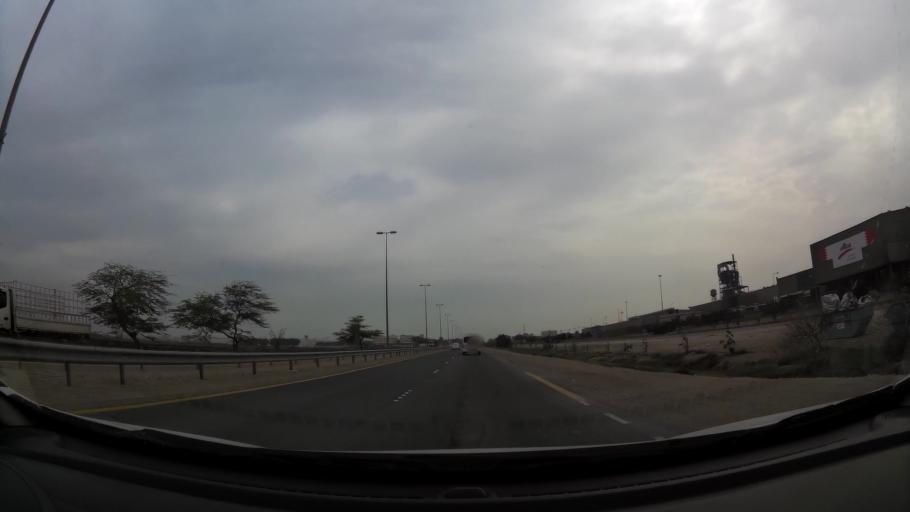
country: BH
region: Northern
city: Sitrah
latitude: 26.0913
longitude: 50.6099
